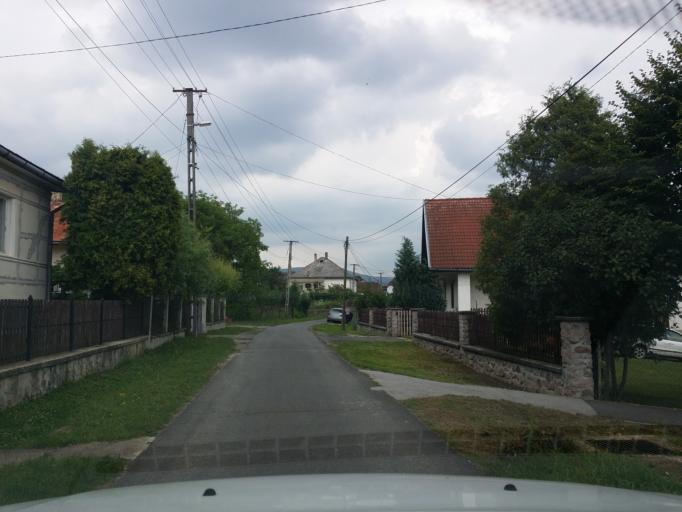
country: HU
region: Borsod-Abauj-Zemplen
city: Sarospatak
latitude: 48.4528
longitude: 21.5267
